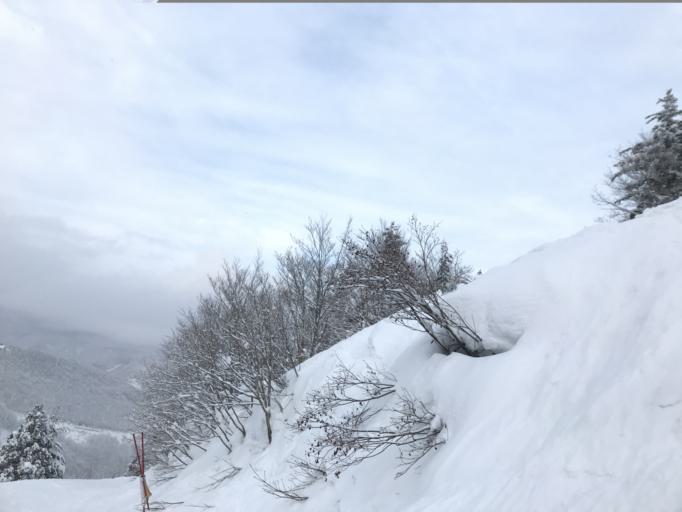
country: JP
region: Nagano
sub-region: Kitaazumi Gun
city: Hakuba
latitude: 36.7009
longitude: 137.8178
